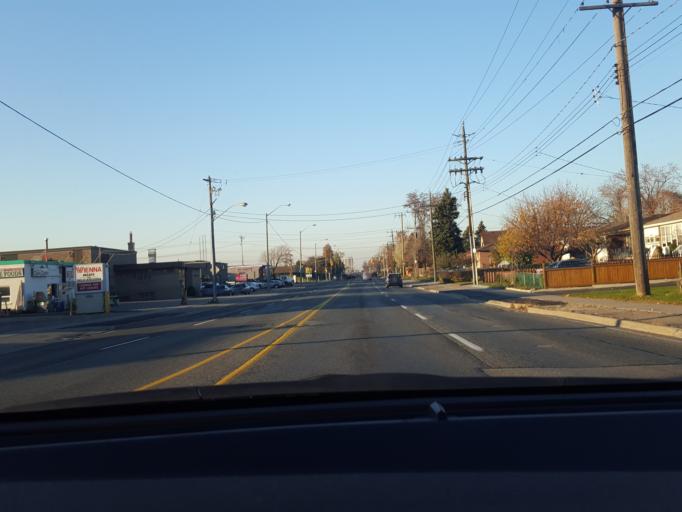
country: CA
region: Ontario
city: Scarborough
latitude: 43.7335
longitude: -79.2791
